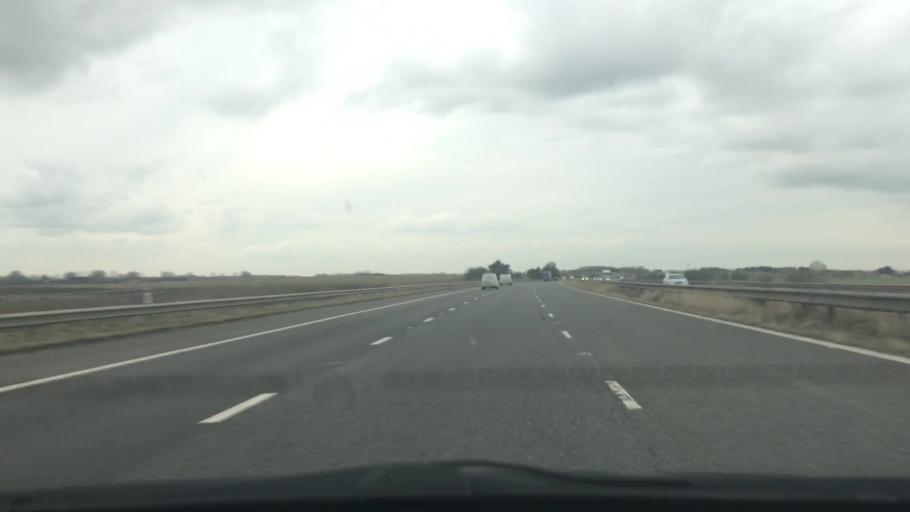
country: GB
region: England
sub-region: Doncaster
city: Hatfield
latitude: 53.5825
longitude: -0.9492
